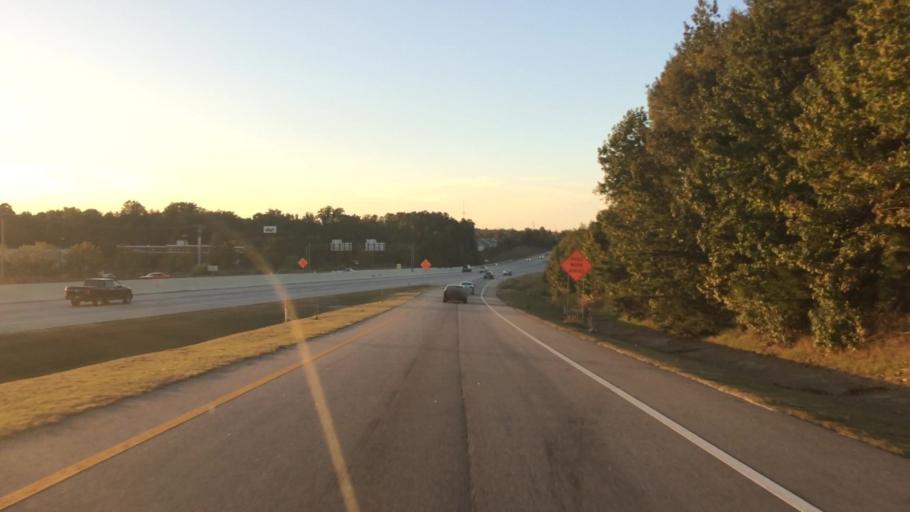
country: US
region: South Carolina
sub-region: Greenville County
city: Mauldin
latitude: 34.8076
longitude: -82.2836
